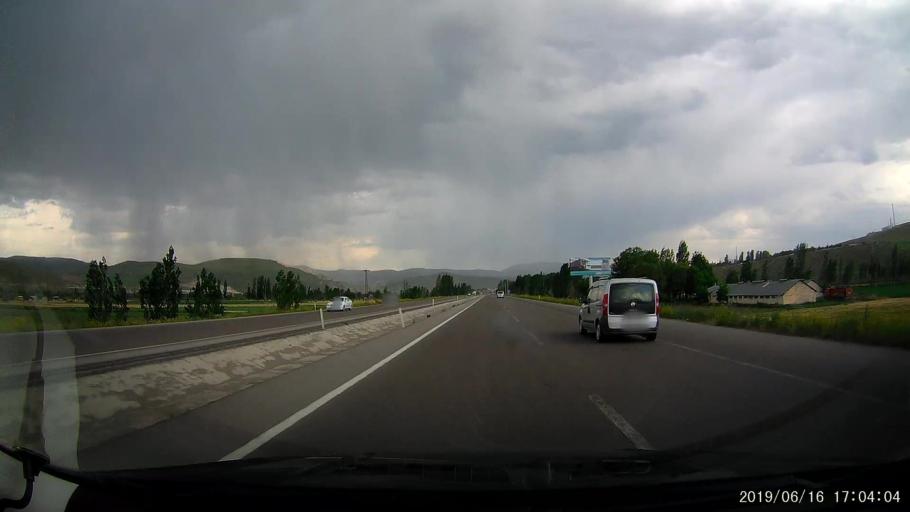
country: TR
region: Erzurum
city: Askale
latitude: 39.9299
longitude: 40.7174
